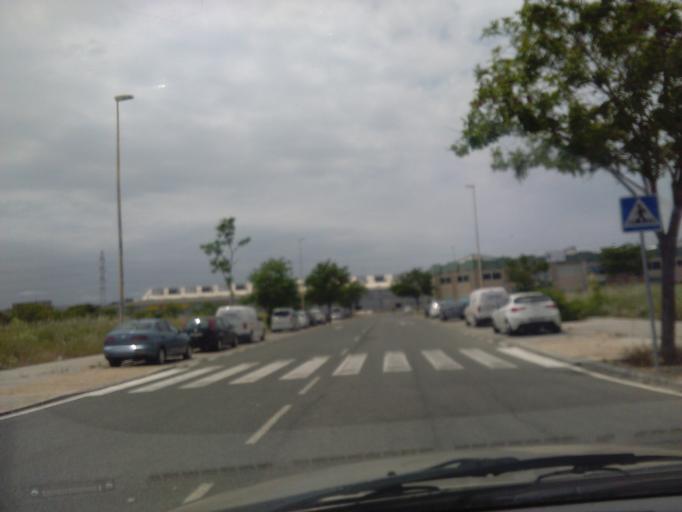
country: ES
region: Andalusia
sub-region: Provincia de Sevilla
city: Sevilla
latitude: 37.3802
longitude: -5.9317
